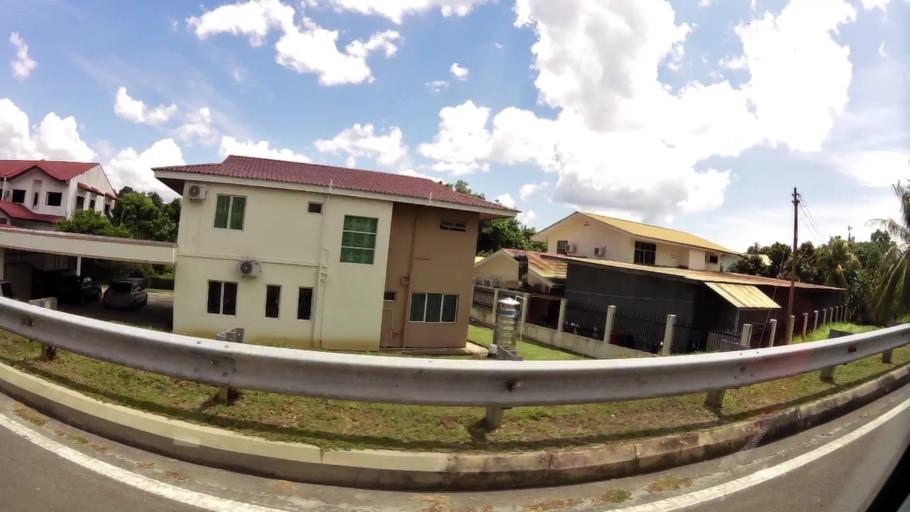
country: BN
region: Brunei and Muara
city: Bandar Seri Begawan
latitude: 4.9452
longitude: 114.9667
